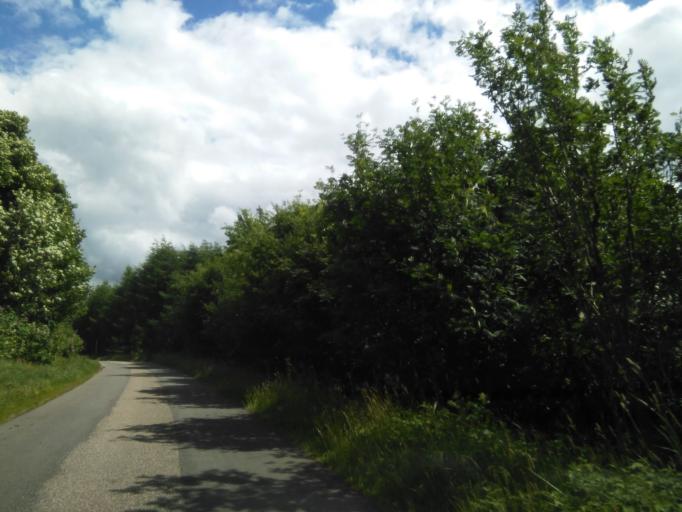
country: DK
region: Central Jutland
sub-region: Silkeborg Kommune
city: Virklund
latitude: 56.0345
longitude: 9.4074
